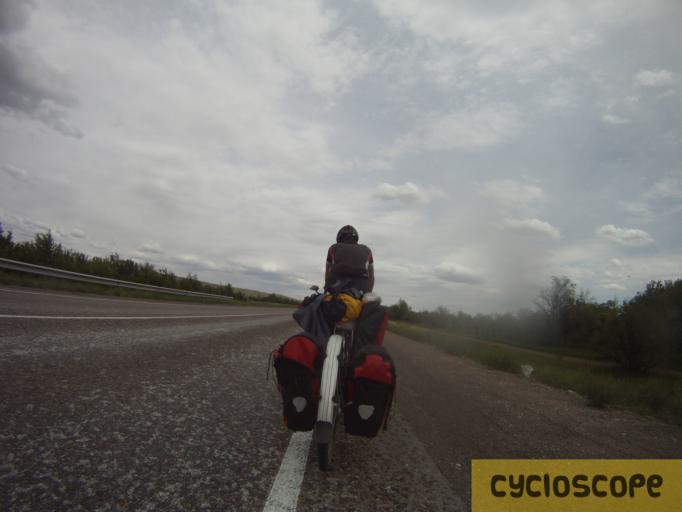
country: KZ
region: Zhambyl
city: Georgiyevka
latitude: 43.3269
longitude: 74.9424
